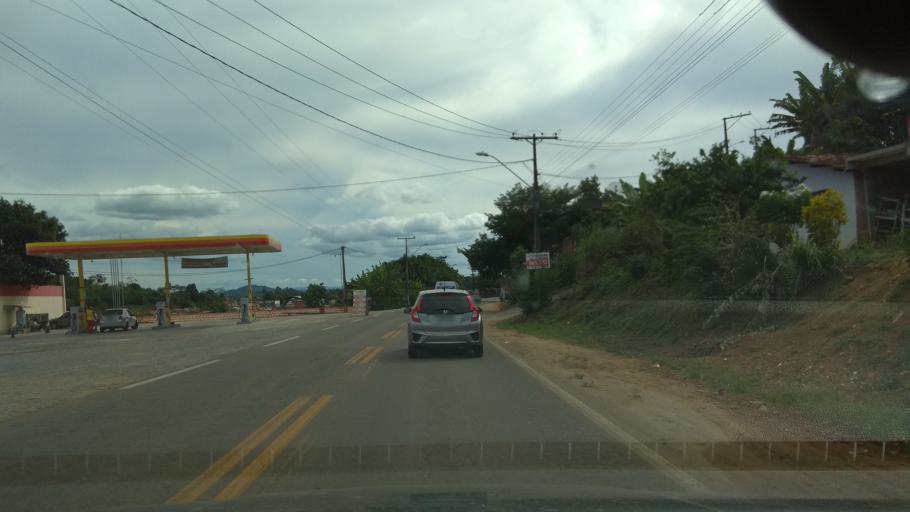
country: BR
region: Bahia
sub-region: Ubata
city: Ubata
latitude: -14.2082
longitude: -39.5994
